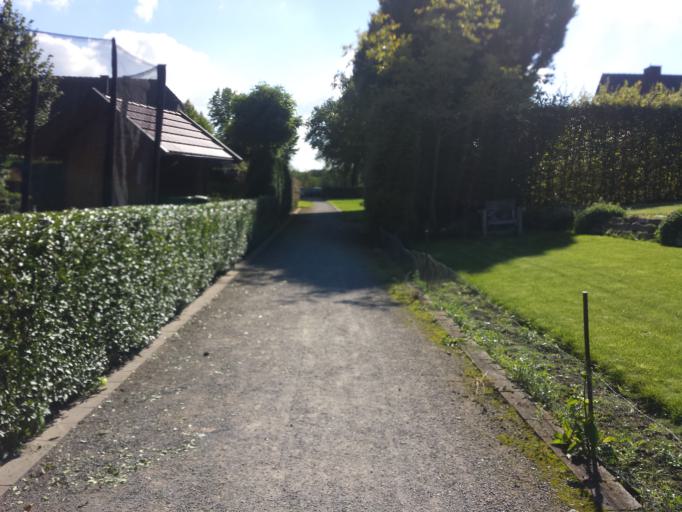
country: DE
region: North Rhine-Westphalia
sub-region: Regierungsbezirk Detmold
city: Langenberg
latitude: 51.7651
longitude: 8.3181
